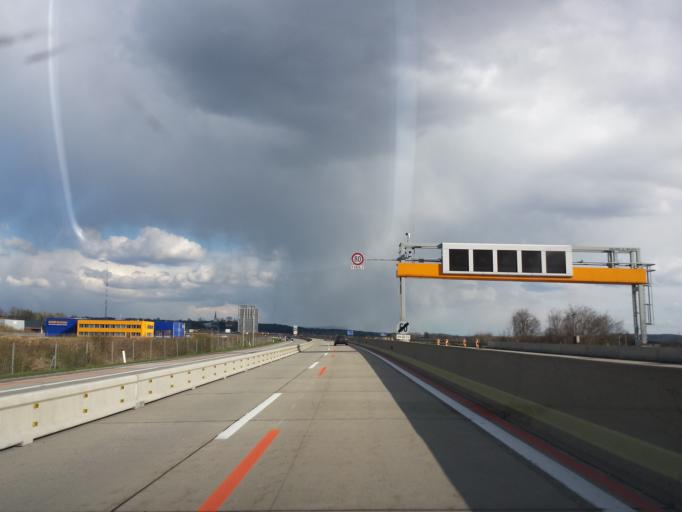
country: AT
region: Styria
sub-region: Politischer Bezirk Deutschlandsberg
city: Lannach
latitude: 46.9560
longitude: 15.3556
